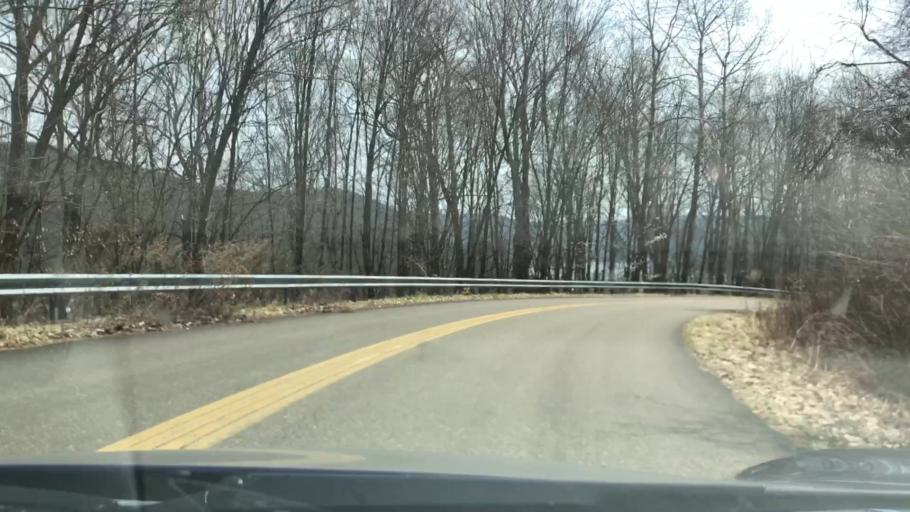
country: US
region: Pennsylvania
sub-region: Warren County
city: Sheffield
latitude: 41.8273
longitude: -78.9577
